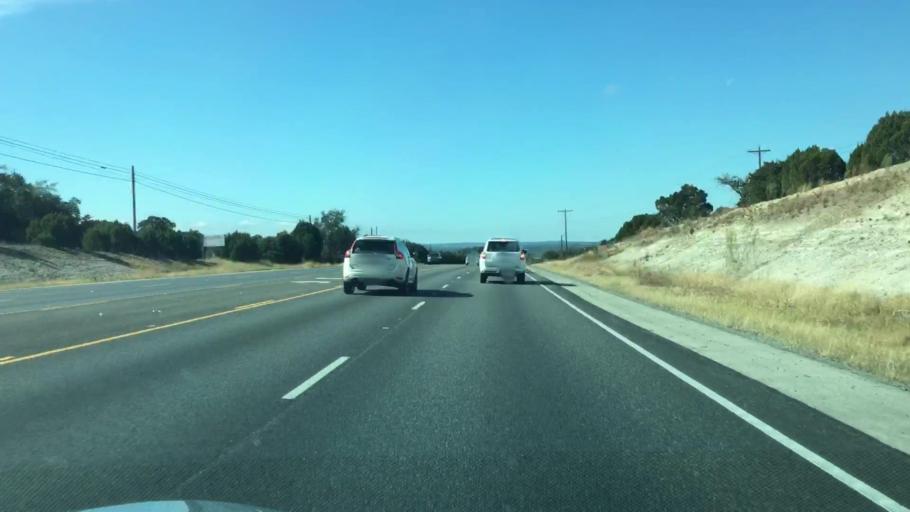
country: US
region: Texas
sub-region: Hays County
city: Dripping Springs
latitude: 30.1912
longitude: -98.0730
